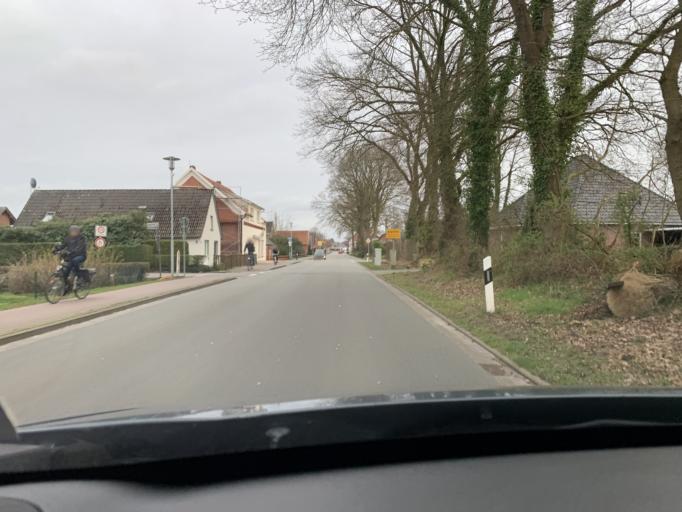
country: DE
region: Lower Saxony
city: Apen
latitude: 53.2240
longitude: 7.7520
